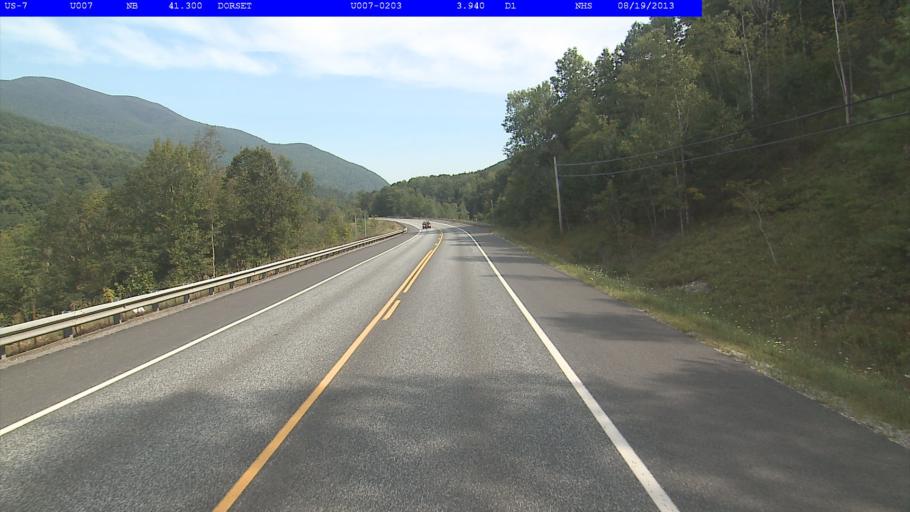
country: US
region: Vermont
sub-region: Bennington County
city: Manchester Center
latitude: 43.2660
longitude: -73.0071
